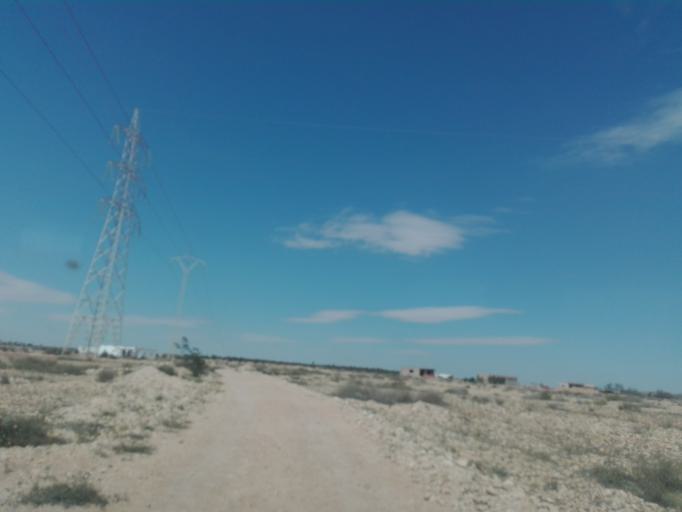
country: TN
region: Safaqis
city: Sfax
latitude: 34.6881
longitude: 10.5352
